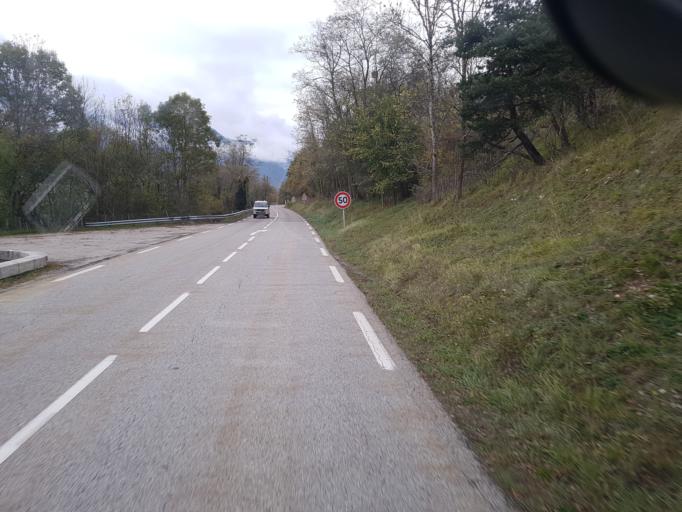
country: FR
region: Rhone-Alpes
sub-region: Departement de l'Isere
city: Le Gua
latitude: 44.9620
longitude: 5.6365
